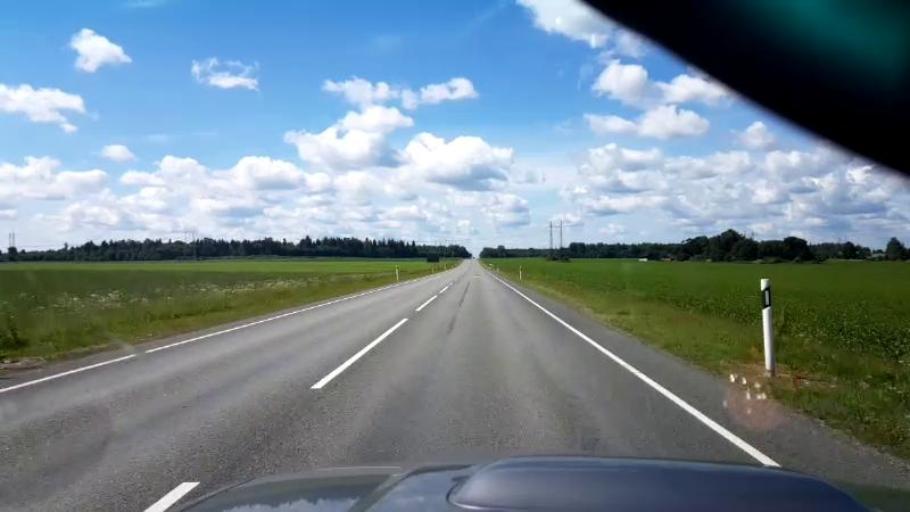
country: EE
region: Laeaene-Virumaa
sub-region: Tapa vald
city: Tapa
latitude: 59.1929
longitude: 25.8199
